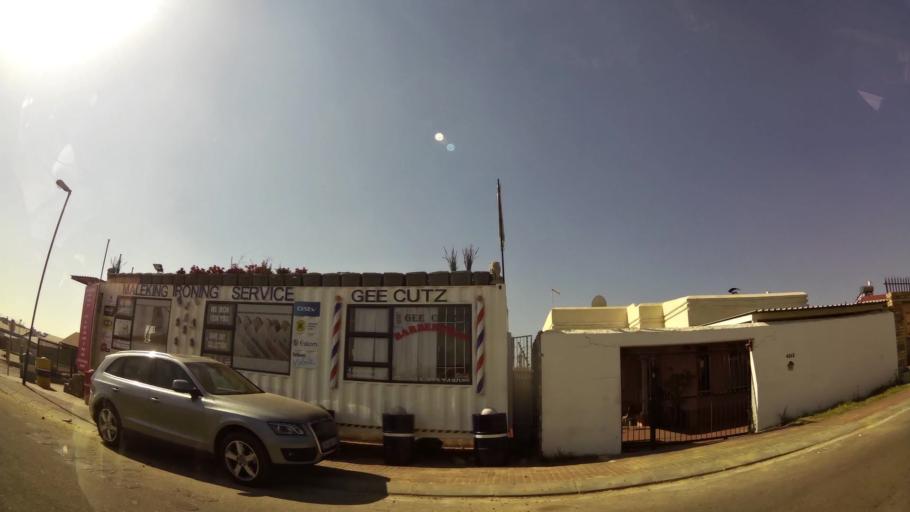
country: ZA
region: Gauteng
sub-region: City of Johannesburg Metropolitan Municipality
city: Johannesburg
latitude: -26.1855
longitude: 27.9802
